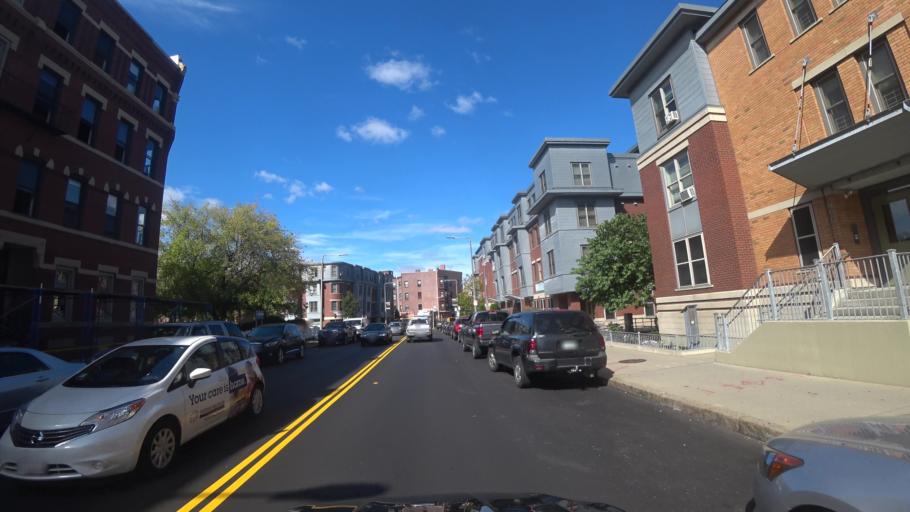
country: US
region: Massachusetts
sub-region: Suffolk County
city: South Boston
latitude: 42.3204
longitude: -71.0715
